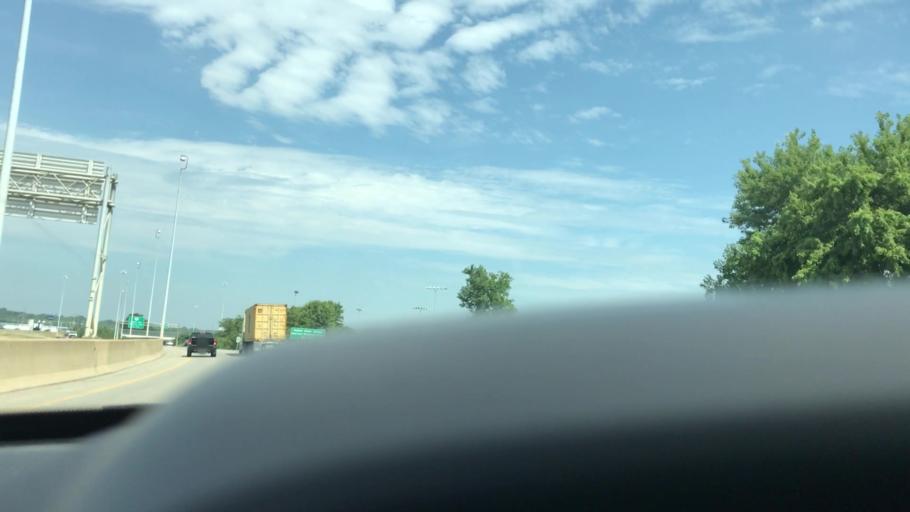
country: US
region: Ohio
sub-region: Stark County
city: Massillon
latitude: 40.7646
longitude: -81.5165
